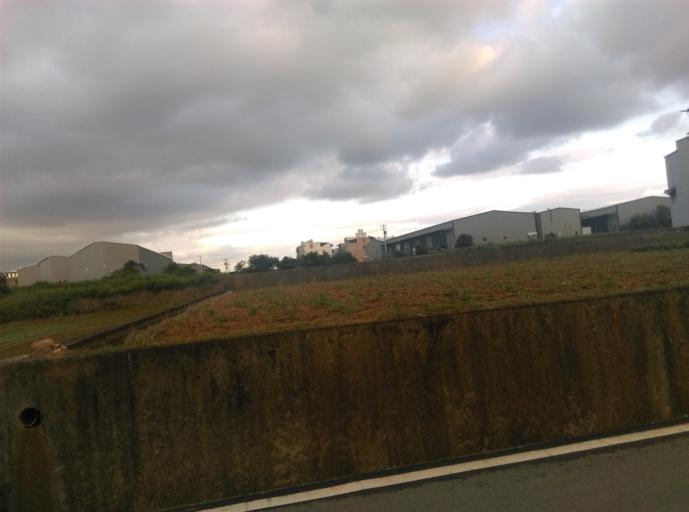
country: TW
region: Taiwan
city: Taoyuan City
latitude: 24.9957
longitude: 121.2511
